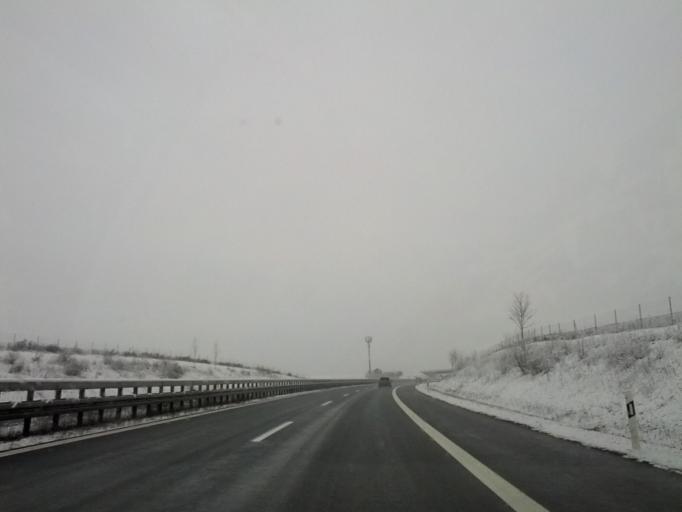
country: DE
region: Bavaria
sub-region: Regierungsbezirk Unterfranken
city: Geldersheim
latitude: 50.0379
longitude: 10.1368
